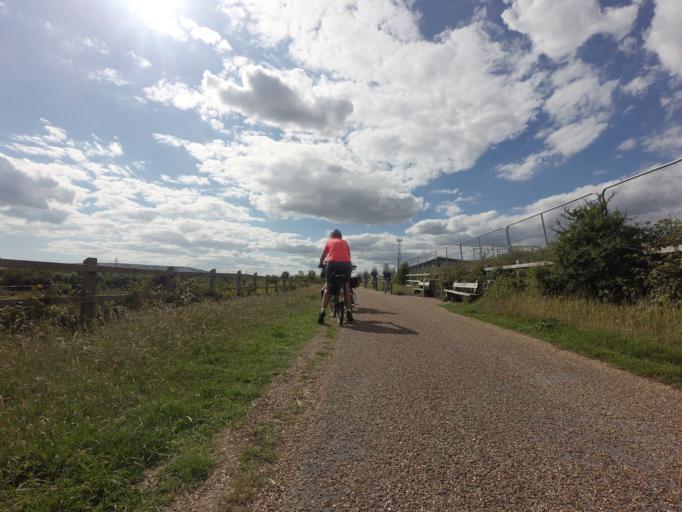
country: GB
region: England
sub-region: East Sussex
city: Hailsham
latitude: 50.8174
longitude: 0.2722
